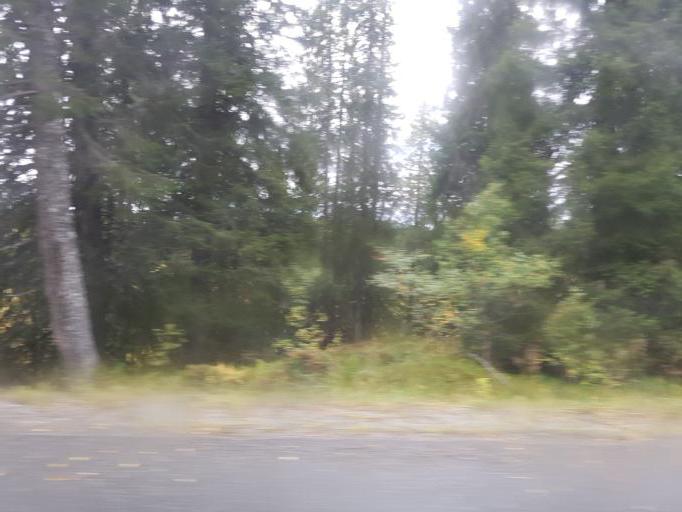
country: NO
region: Sor-Trondelag
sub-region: Melhus
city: Melhus
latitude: 63.4159
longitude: 10.2646
